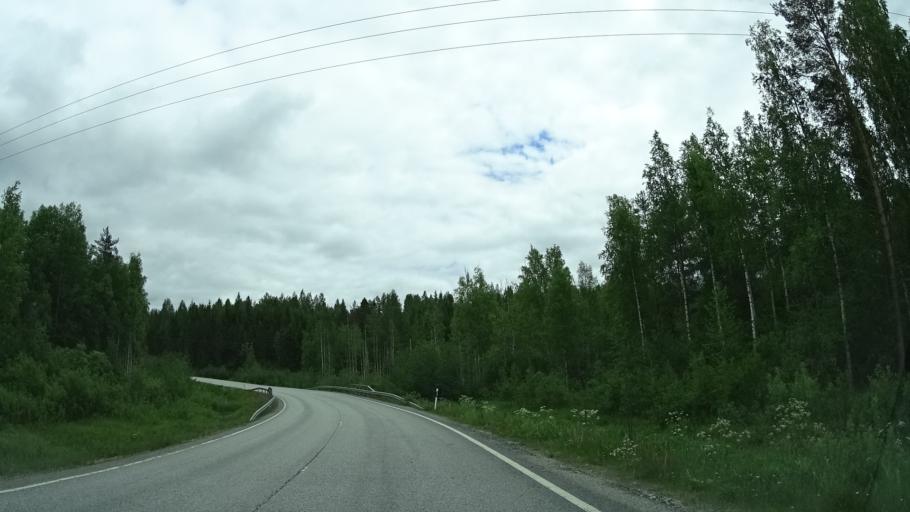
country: FI
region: Central Finland
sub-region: Jyvaeskylae
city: Toivakka
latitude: 62.0775
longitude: 26.0374
